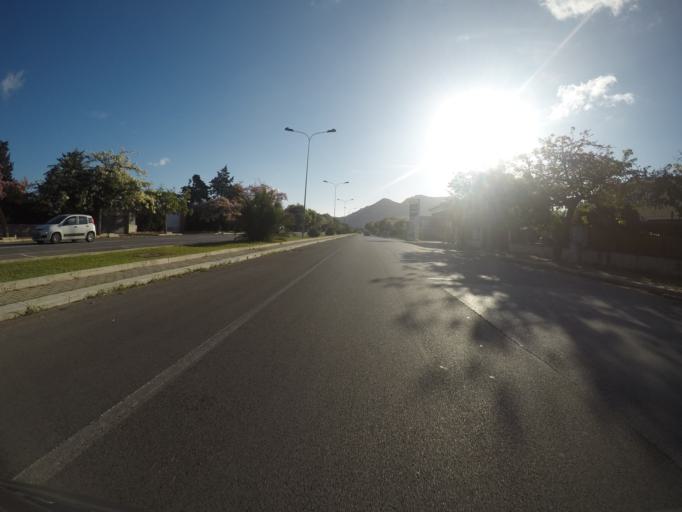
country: IT
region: Sicily
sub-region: Palermo
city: Isola delle Femmine
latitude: 38.1889
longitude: 13.3054
